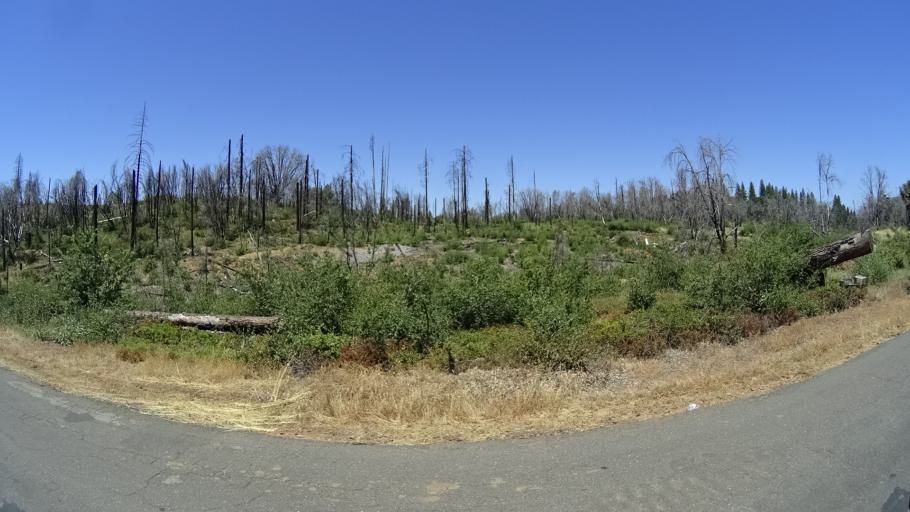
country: US
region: California
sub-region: Calaveras County
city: Mountain Ranch
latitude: 38.2402
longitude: -120.5645
